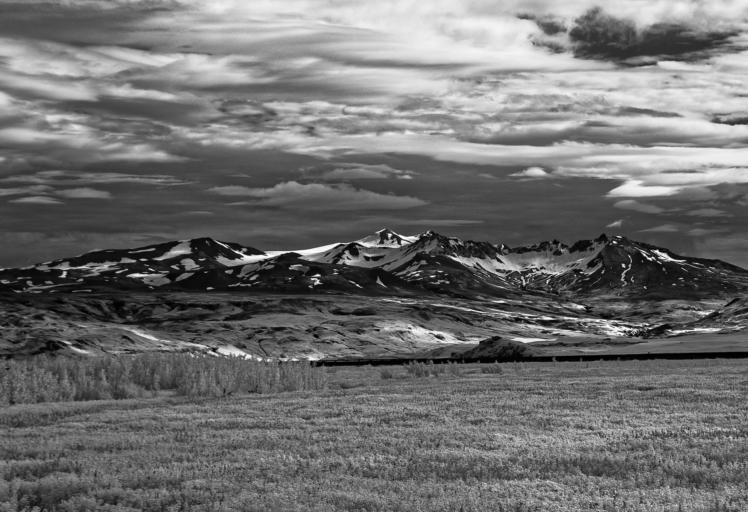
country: IS
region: South
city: Vestmannaeyjar
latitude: 63.6251
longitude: -20.0326
